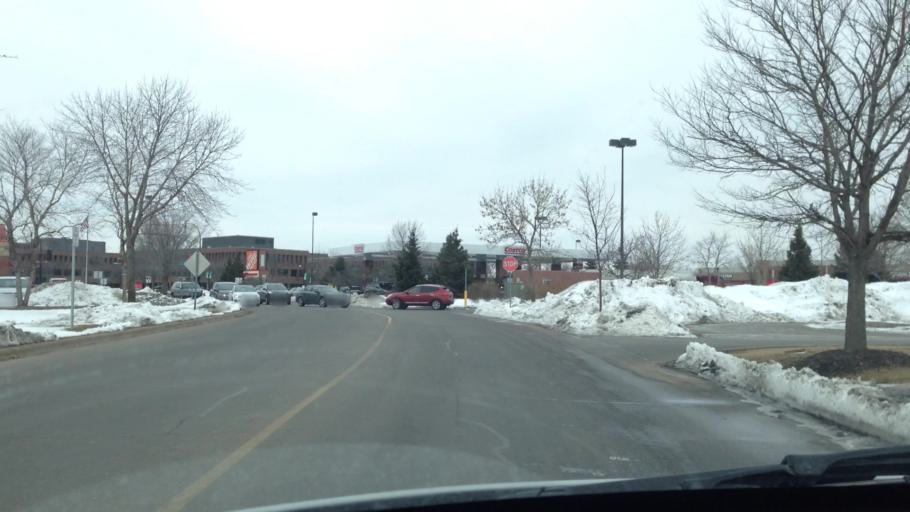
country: US
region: Minnesota
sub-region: Hennepin County
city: Saint Louis Park
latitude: 44.9660
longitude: -93.3512
